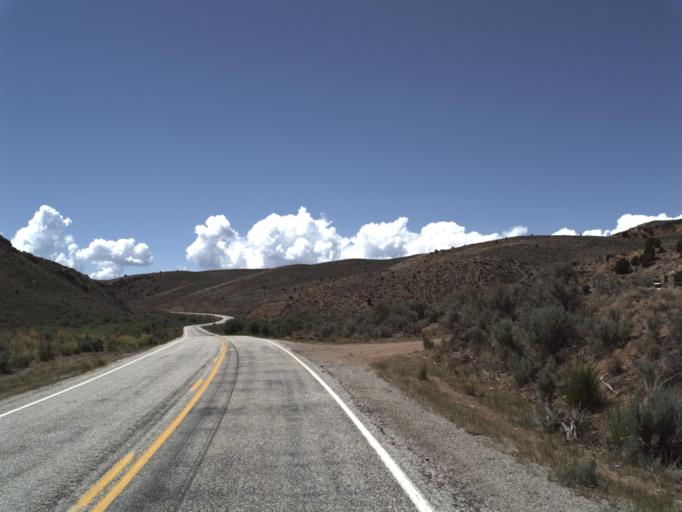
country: US
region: Utah
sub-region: Rich County
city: Randolph
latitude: 41.4998
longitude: -111.2766
